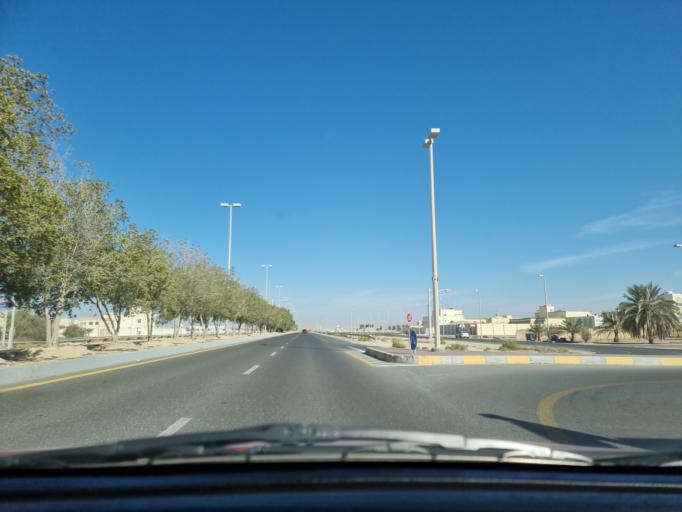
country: AE
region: Abu Dhabi
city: Abu Dhabi
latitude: 24.3936
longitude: 54.6943
